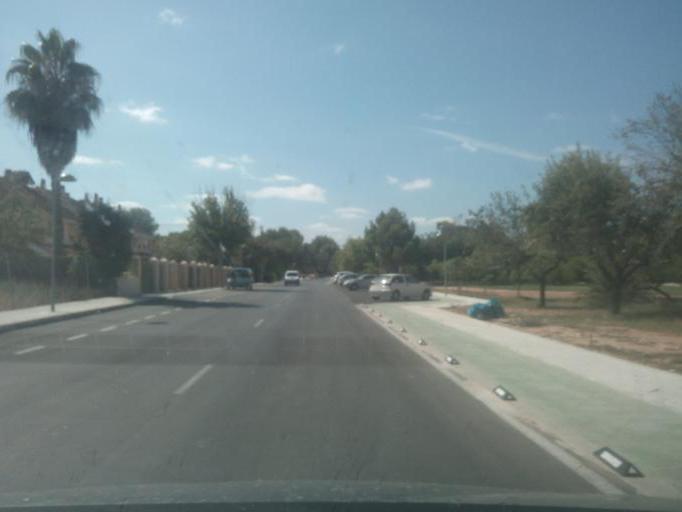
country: ES
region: Valencia
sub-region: Provincia de Valencia
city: Manises
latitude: 39.5354
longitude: -0.4905
